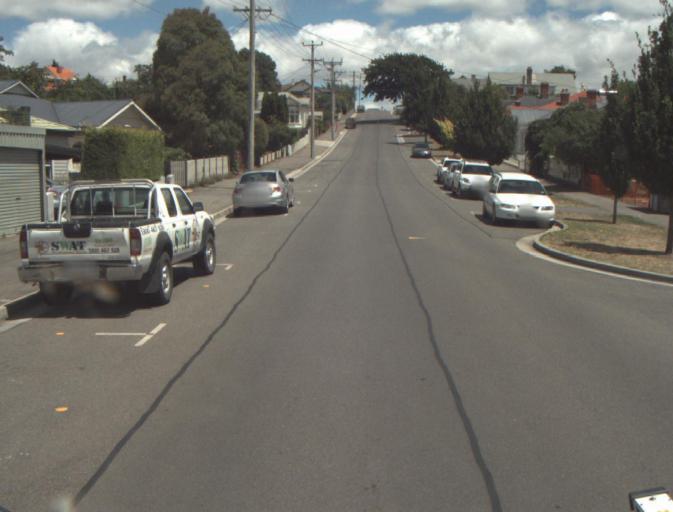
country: AU
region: Tasmania
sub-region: Launceston
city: East Launceston
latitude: -41.4430
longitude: 147.1515
